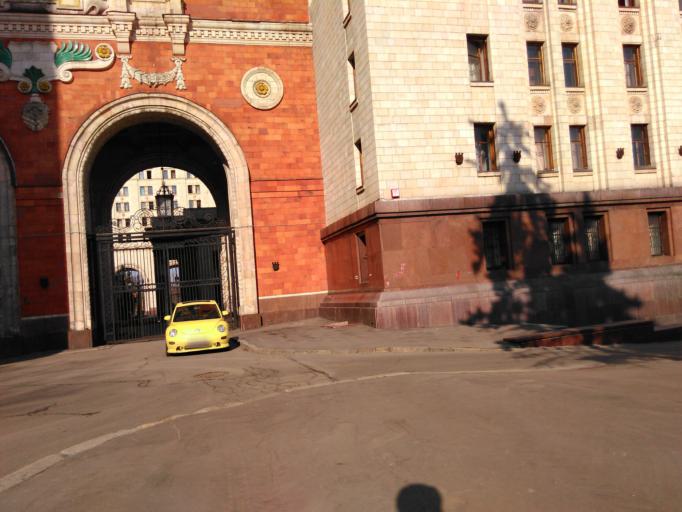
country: RU
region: Moscow
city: Vorob'yovo
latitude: 55.7033
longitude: 37.5286
